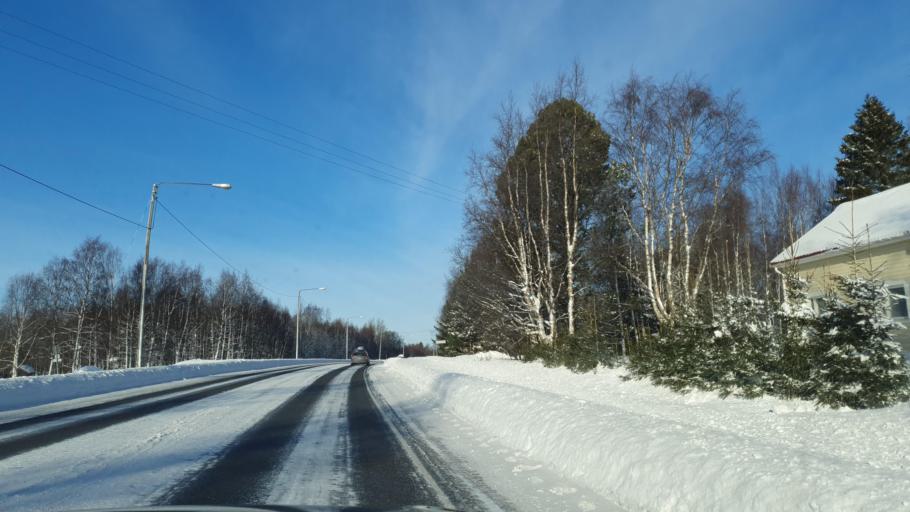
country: FI
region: Lapland
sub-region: Kemi-Tornio
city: Tornio
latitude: 65.8957
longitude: 24.1422
